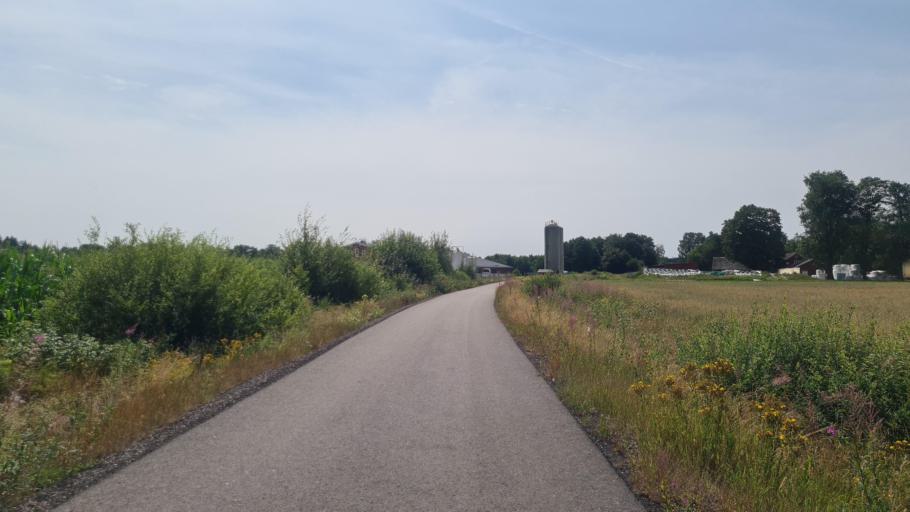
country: SE
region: Kronoberg
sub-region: Ljungby Kommun
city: Lagan
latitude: 56.8746
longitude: 13.9835
